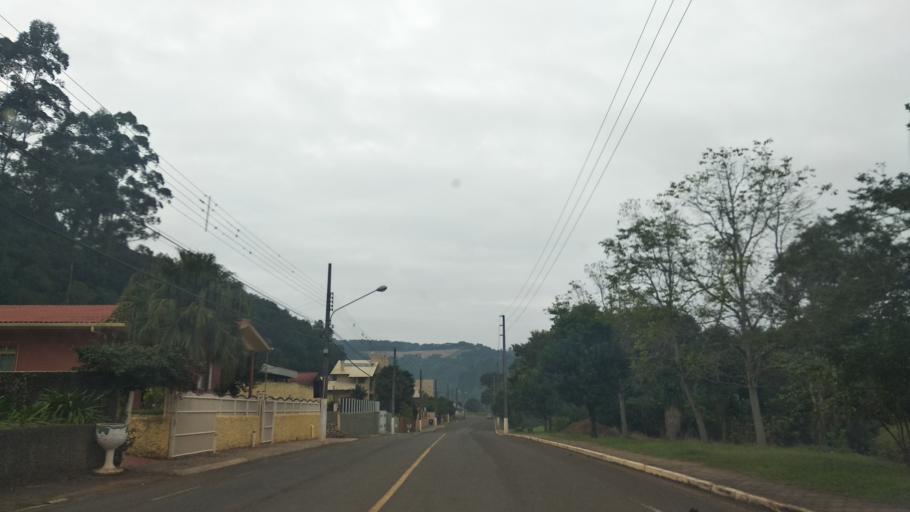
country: BR
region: Santa Catarina
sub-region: Videira
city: Videira
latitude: -27.0518
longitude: -51.2316
